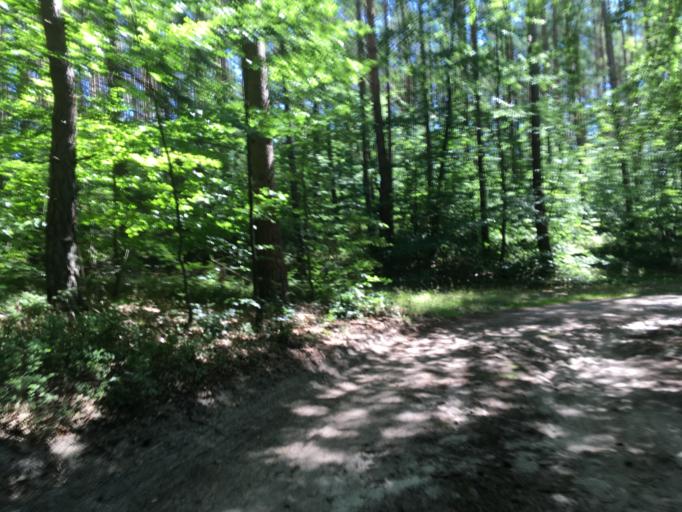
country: DE
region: Brandenburg
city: Rheinsberg
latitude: 53.1183
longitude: 13.0028
